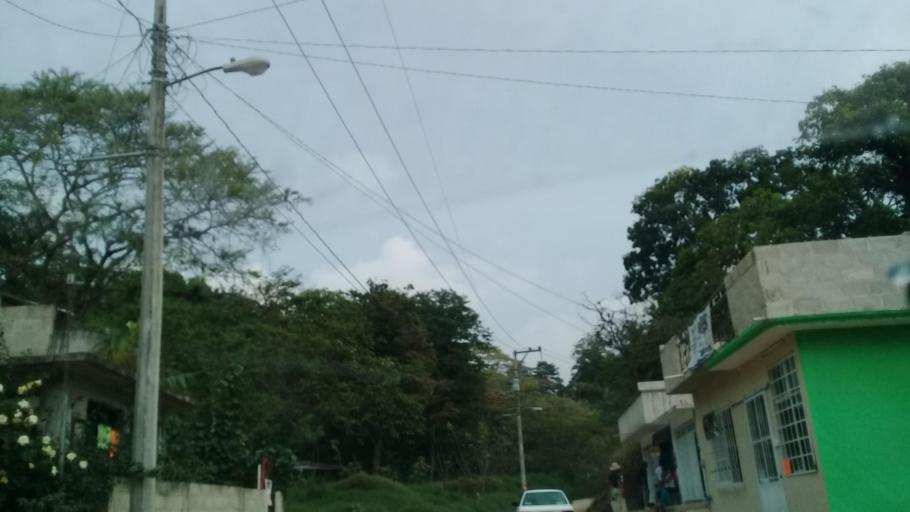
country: MX
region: Veracruz
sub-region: Xalapa
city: Fraccionamiento las Fuentes
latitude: 19.4956
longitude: -96.8988
